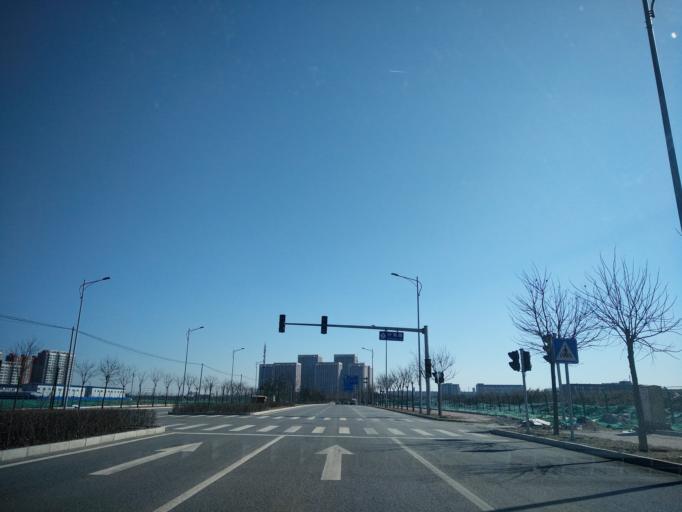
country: CN
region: Beijing
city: Yinghai
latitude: 39.7511
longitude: 116.4859
